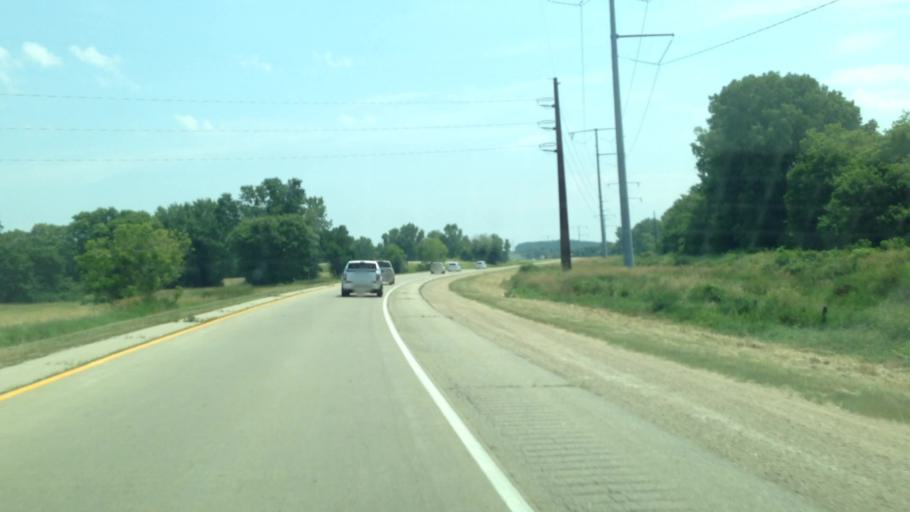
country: US
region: Wisconsin
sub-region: Dane County
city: McFarland
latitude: 43.0460
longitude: -89.2829
